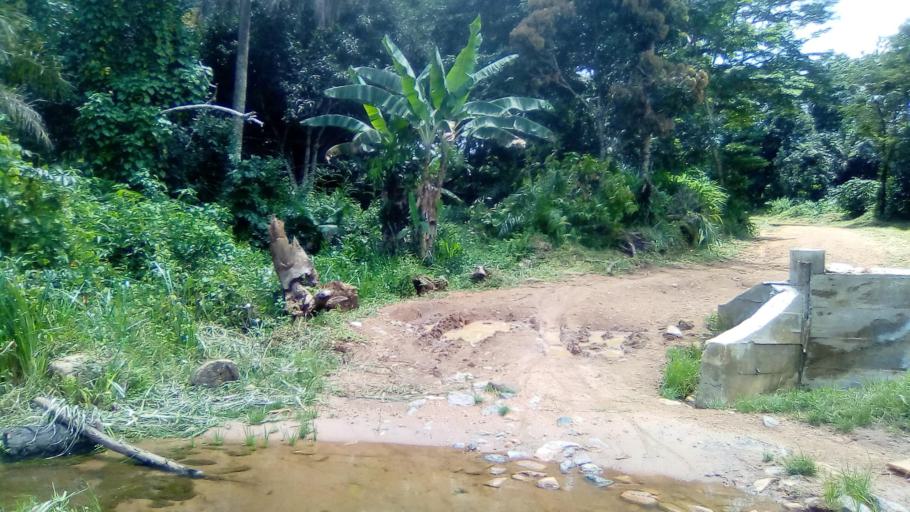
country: SL
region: Eastern Province
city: Giehun
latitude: 8.4993
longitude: -10.9080
